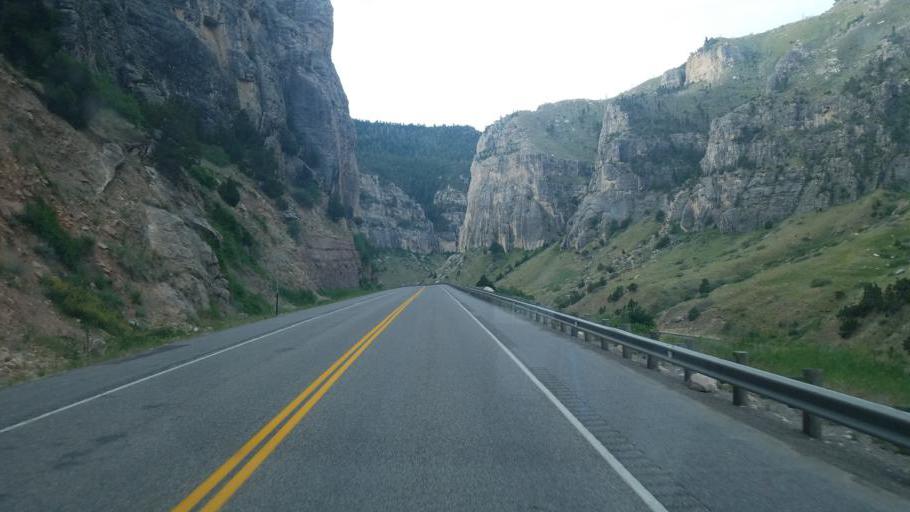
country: US
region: Wyoming
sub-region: Hot Springs County
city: Thermopolis
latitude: 43.5328
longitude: -108.1788
